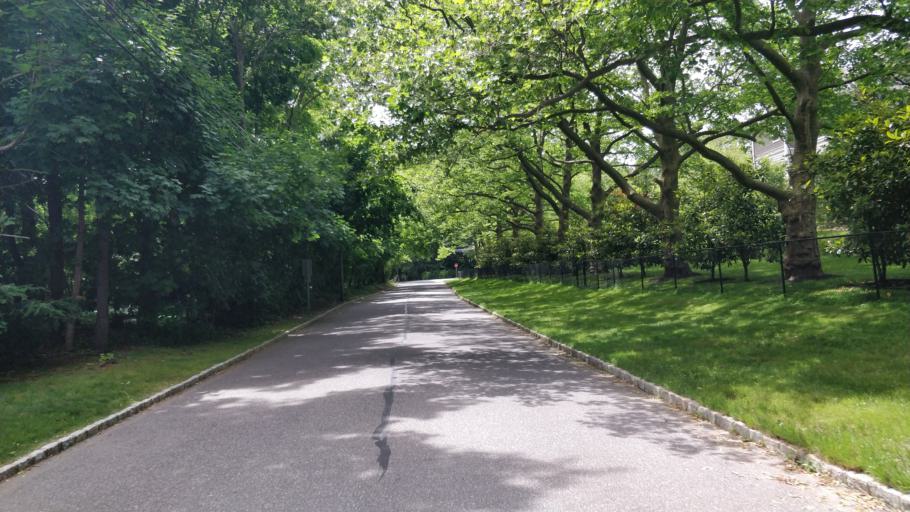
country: US
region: New York
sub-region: Nassau County
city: Laurel Hollow
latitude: 40.8409
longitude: -73.4788
